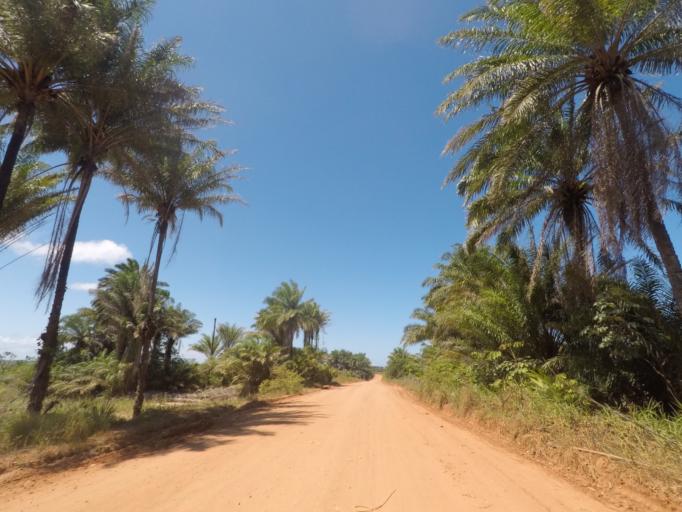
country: BR
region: Bahia
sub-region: Camamu
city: Camamu
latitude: -13.9562
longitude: -38.9459
